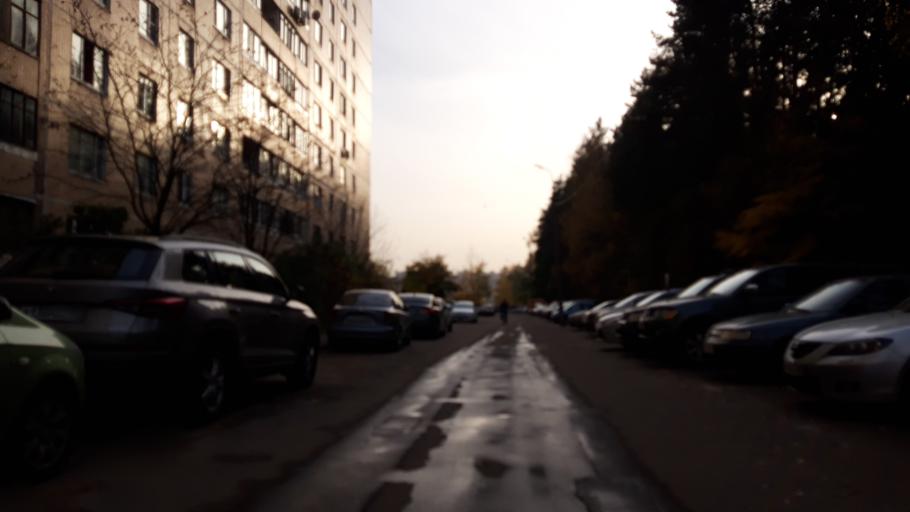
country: RU
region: Moscow
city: Zelenograd
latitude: 55.9953
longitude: 37.1702
